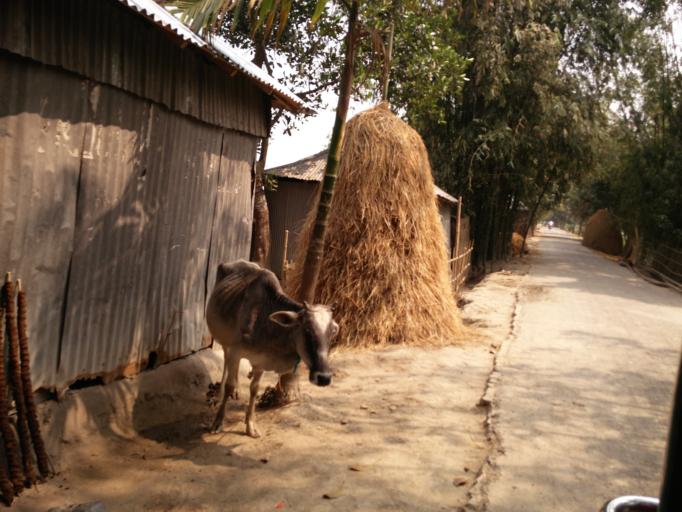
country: BD
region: Rangpur Division
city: Nageswari
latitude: 25.8892
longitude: 89.7227
